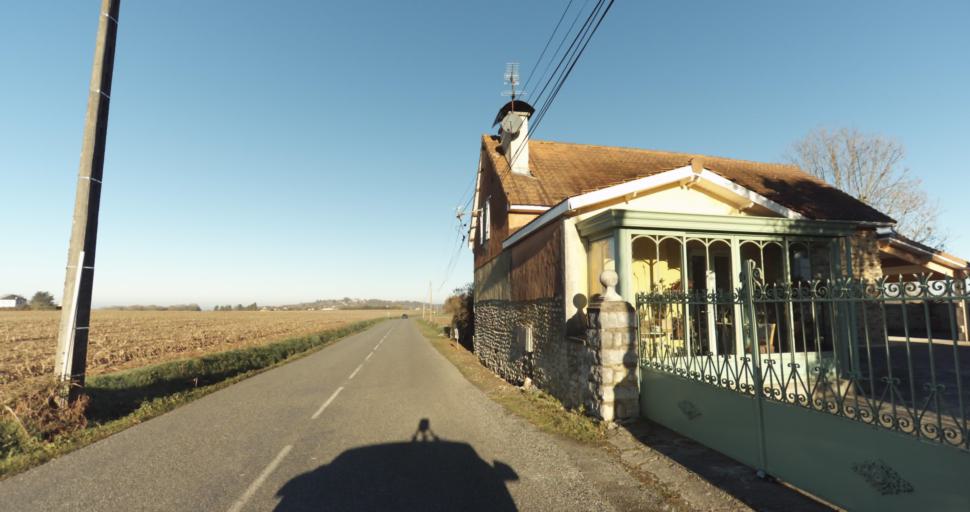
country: FR
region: Aquitaine
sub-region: Departement des Pyrenees-Atlantiques
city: Ousse
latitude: 43.3123
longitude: -0.2348
